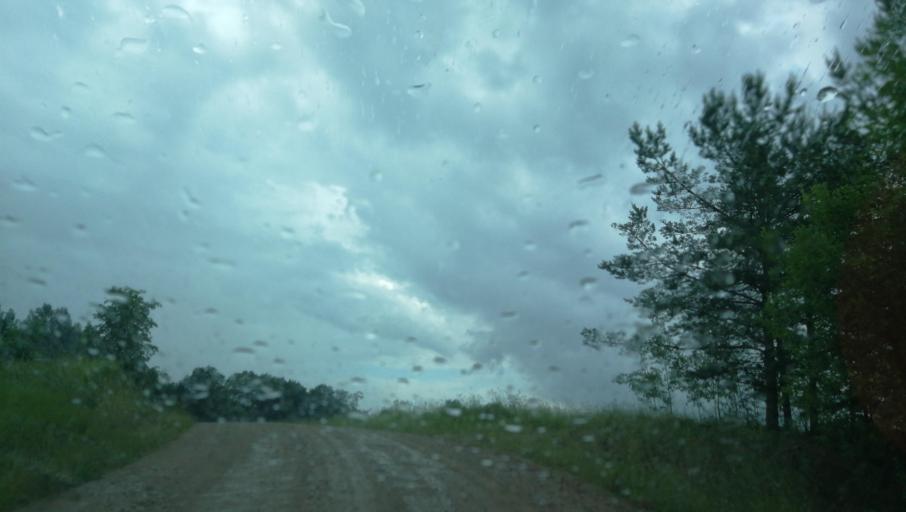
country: LV
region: Vecpiebalga
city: Vecpiebalga
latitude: 57.0990
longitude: 25.6906
